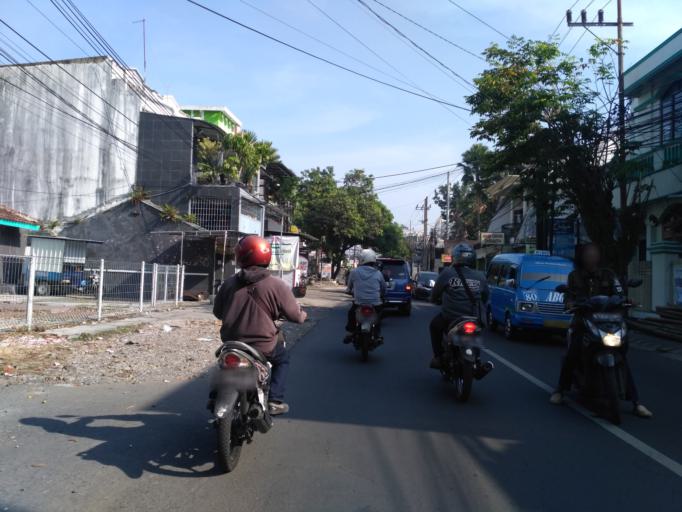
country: ID
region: East Java
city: Malang
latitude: -7.9458
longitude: 112.6214
